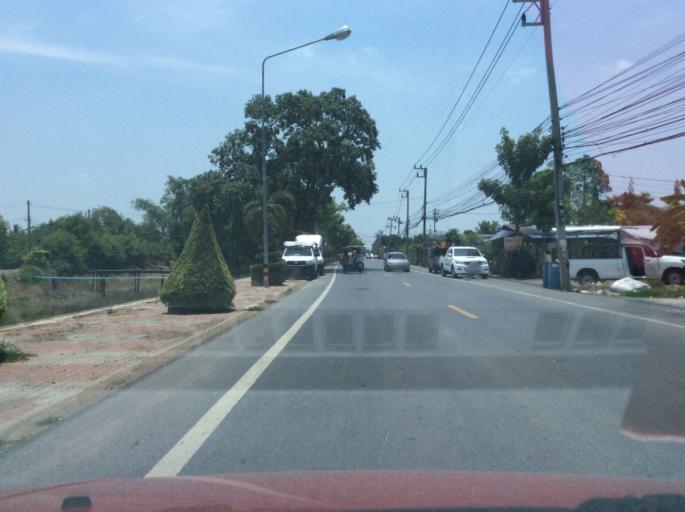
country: TH
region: Pathum Thani
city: Lam Luk Ka
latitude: 13.9591
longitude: 100.7276
